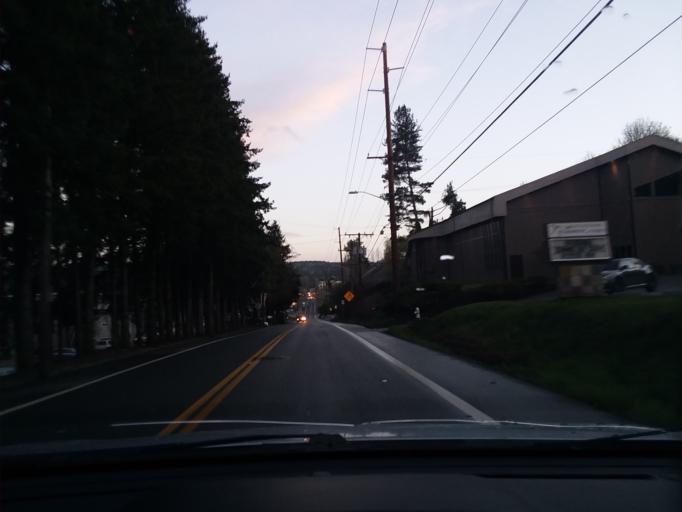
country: US
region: Washington
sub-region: King County
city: Kenmore
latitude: 47.7659
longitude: -122.2496
